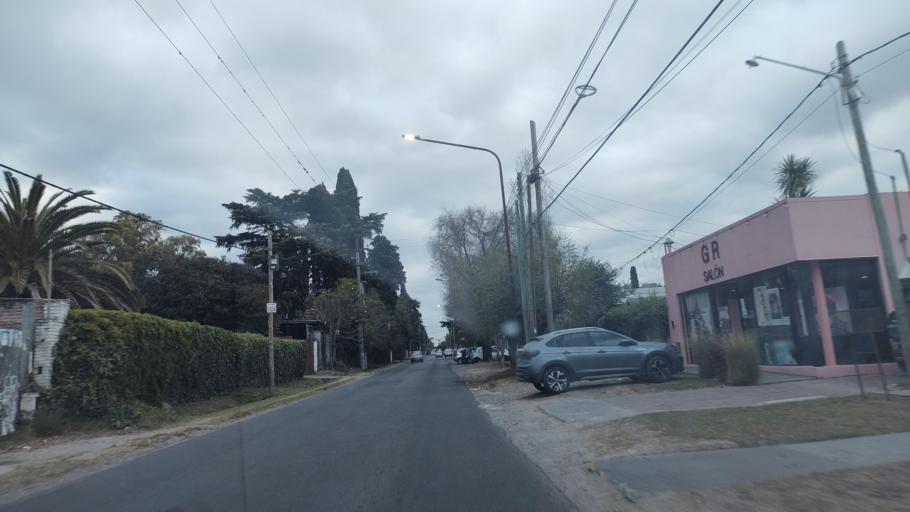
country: AR
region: Buenos Aires
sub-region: Partido de La Plata
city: La Plata
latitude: -34.8674
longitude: -58.0954
